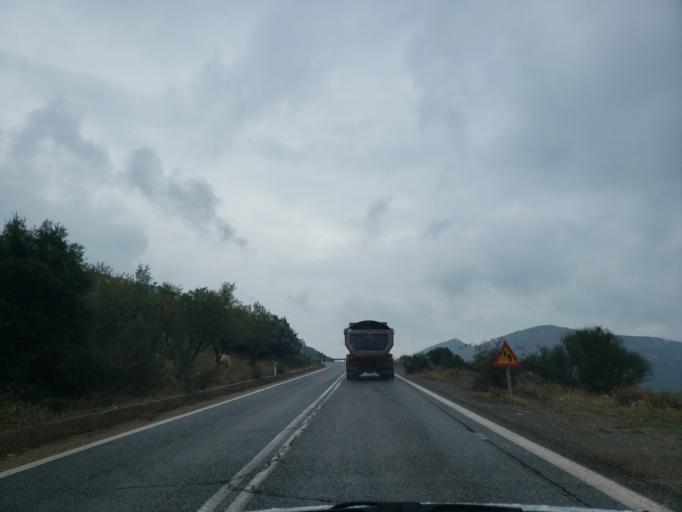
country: GR
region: Central Greece
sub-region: Nomos Fokidos
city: Amfissa
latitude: 38.5847
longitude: 22.3909
